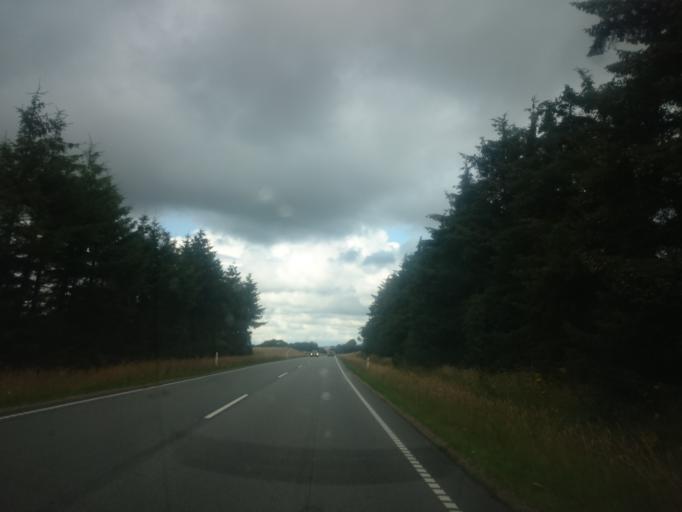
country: DK
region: South Denmark
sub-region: Billund Kommune
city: Grindsted
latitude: 55.6831
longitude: 8.9625
